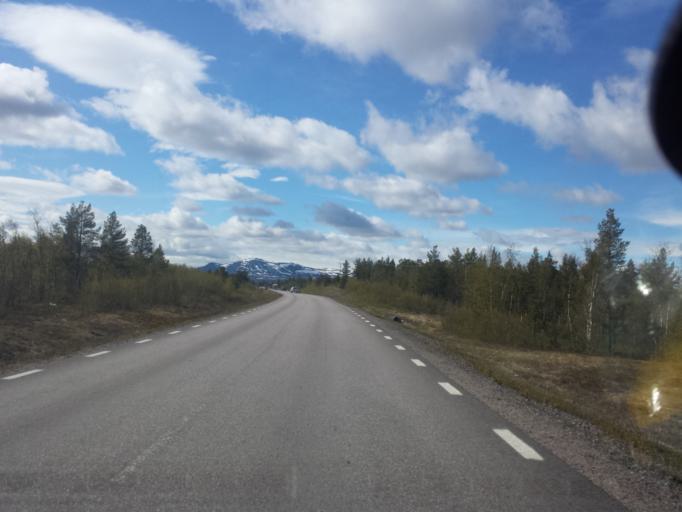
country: SE
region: Norrbotten
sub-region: Kiruna Kommun
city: Kiruna
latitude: 67.9888
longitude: 19.9316
